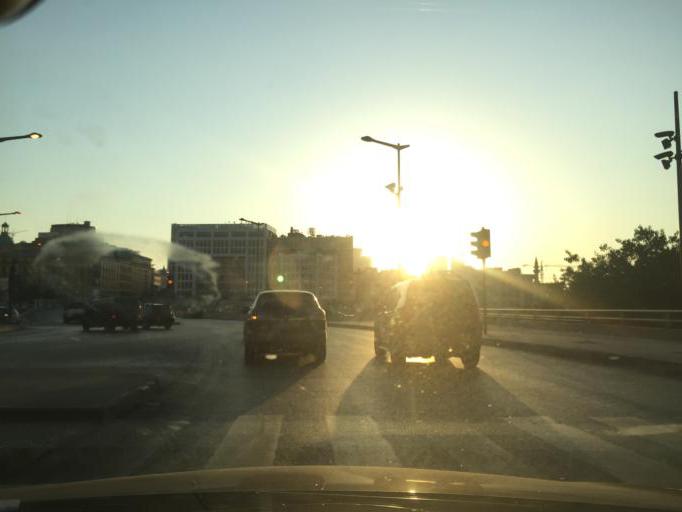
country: LB
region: Beyrouth
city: Beirut
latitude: 33.8973
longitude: 35.5099
